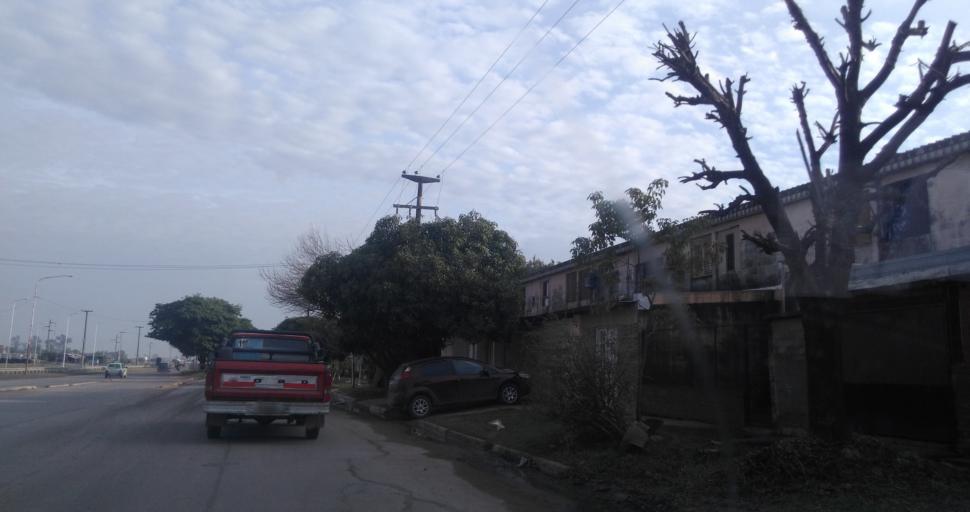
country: AR
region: Chaco
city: Resistencia
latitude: -27.4634
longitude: -59.0157
